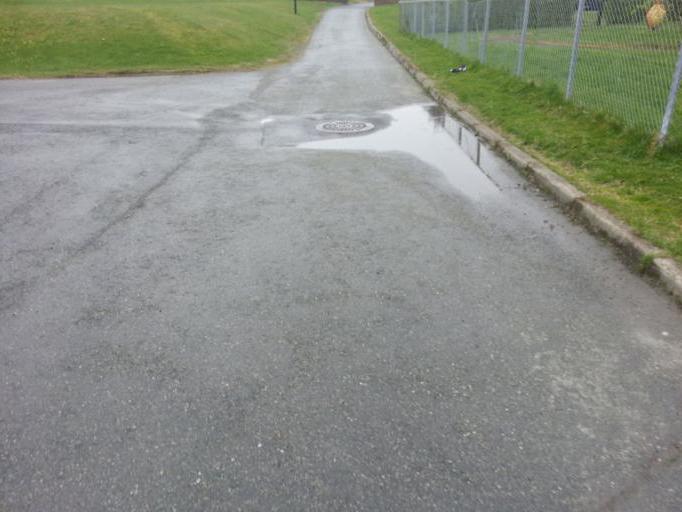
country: NO
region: Sor-Trondelag
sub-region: Trondheim
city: Trondheim
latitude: 63.3898
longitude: 10.3469
